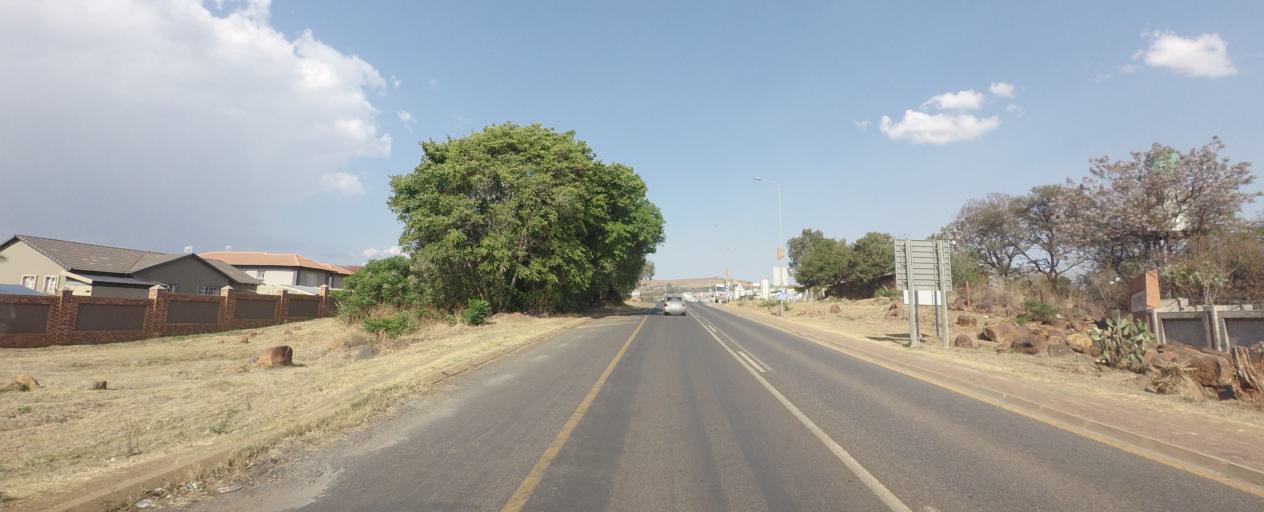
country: ZA
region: Mpumalanga
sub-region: Ehlanzeni District
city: Lydenburg
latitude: -25.1031
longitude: 30.4764
